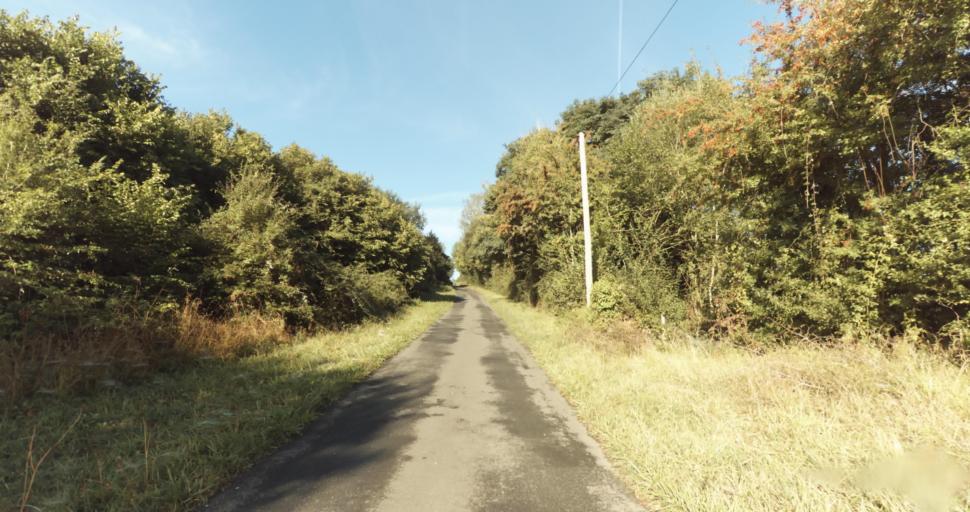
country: FR
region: Lower Normandy
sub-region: Departement de l'Orne
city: Vimoutiers
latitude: 48.9168
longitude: 0.1853
